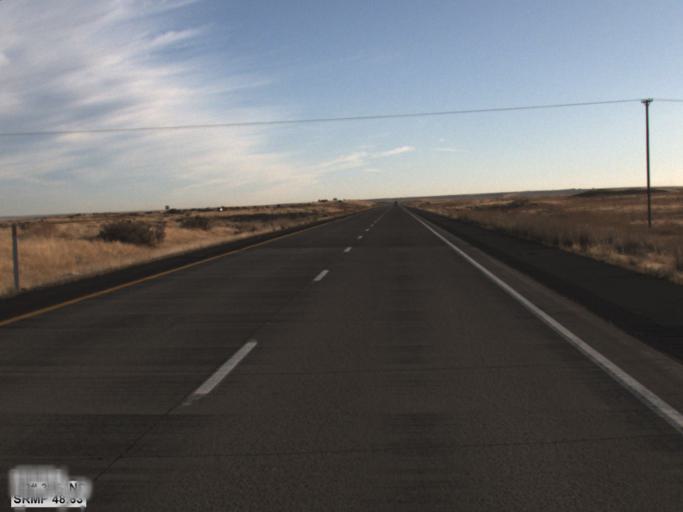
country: US
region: Washington
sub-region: Franklin County
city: Connell
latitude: 46.5945
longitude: -118.9519
